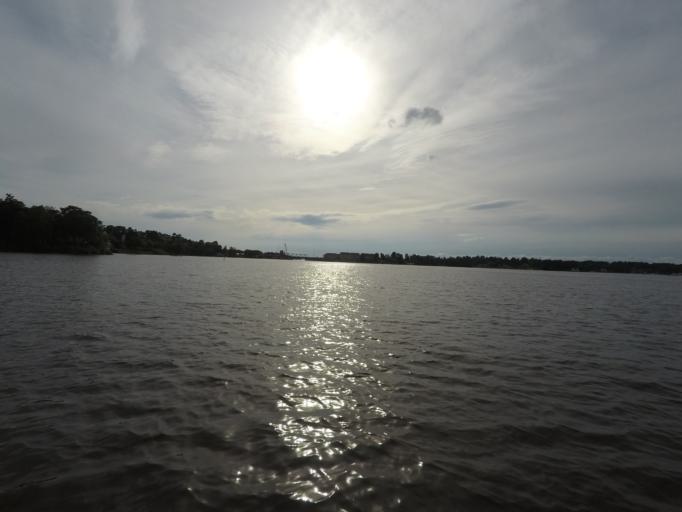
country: SE
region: Soedermanland
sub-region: Eskilstuna Kommun
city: Kvicksund
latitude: 59.4535
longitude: 16.3320
